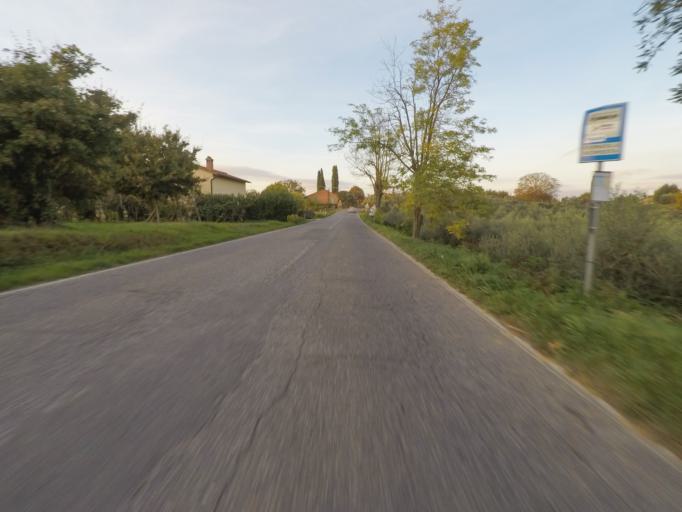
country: IT
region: Tuscany
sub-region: Provincia di Siena
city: Montepulciano
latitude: 43.1298
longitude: 11.7280
